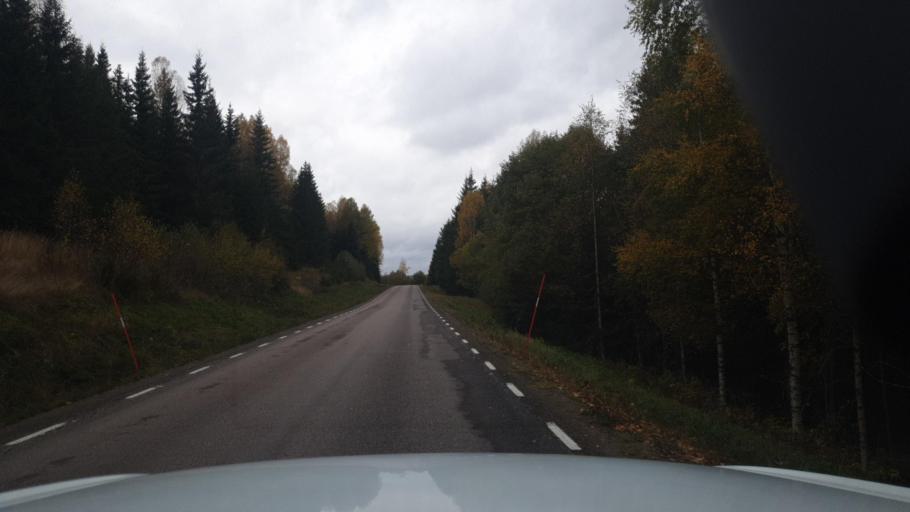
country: SE
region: Vaermland
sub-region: Torsby Kommun
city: Torsby
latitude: 59.9316
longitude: 12.8351
